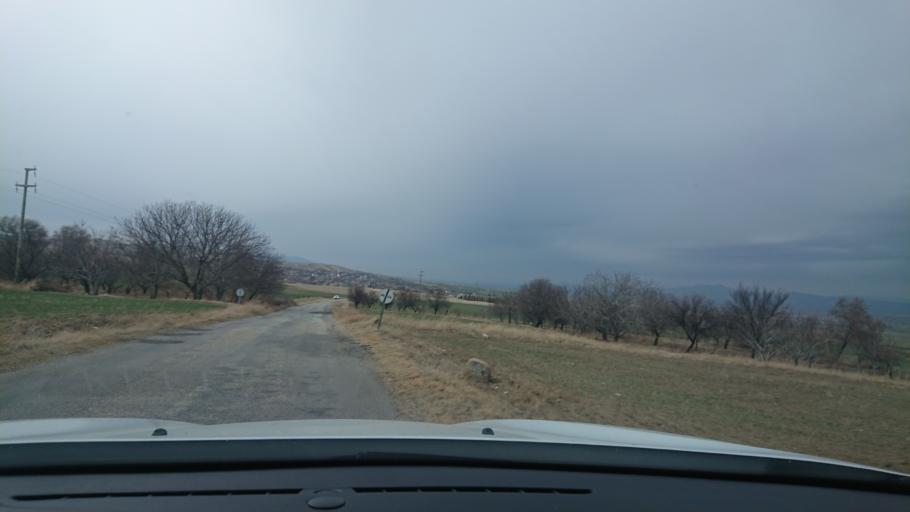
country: TR
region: Aksaray
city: Agacoren
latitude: 38.9466
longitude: 33.9068
